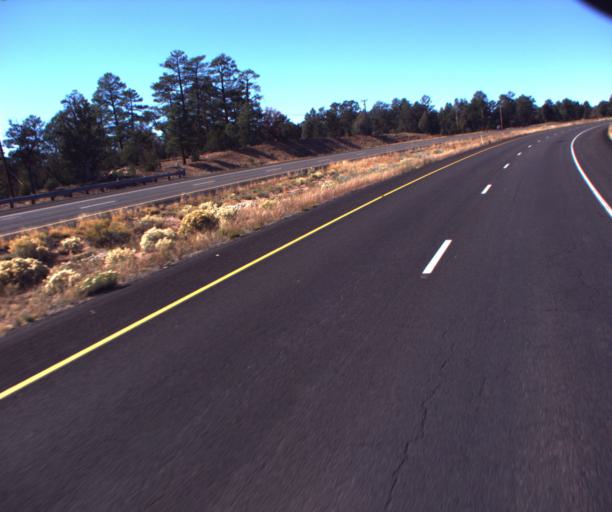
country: US
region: Arizona
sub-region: Apache County
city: Saint Michaels
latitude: 35.6571
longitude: -109.1542
